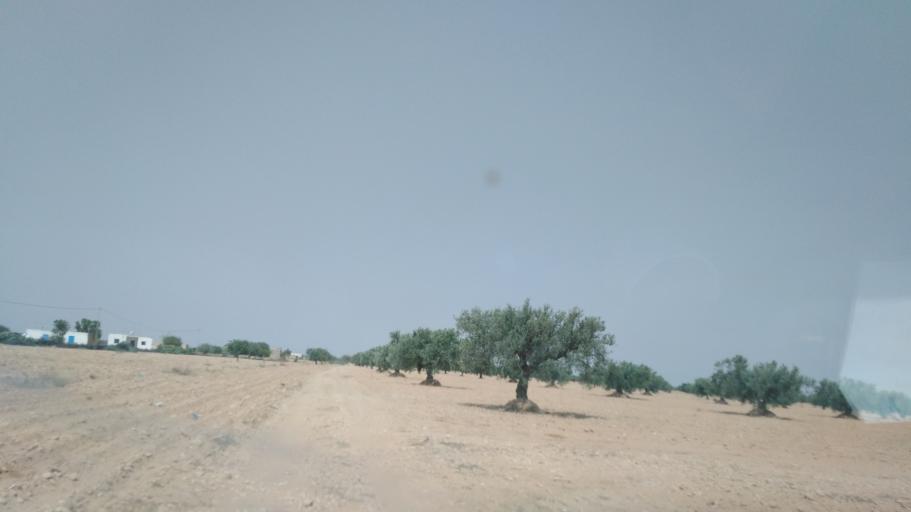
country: TN
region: Safaqis
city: Sfax
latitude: 34.6538
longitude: 10.5565
